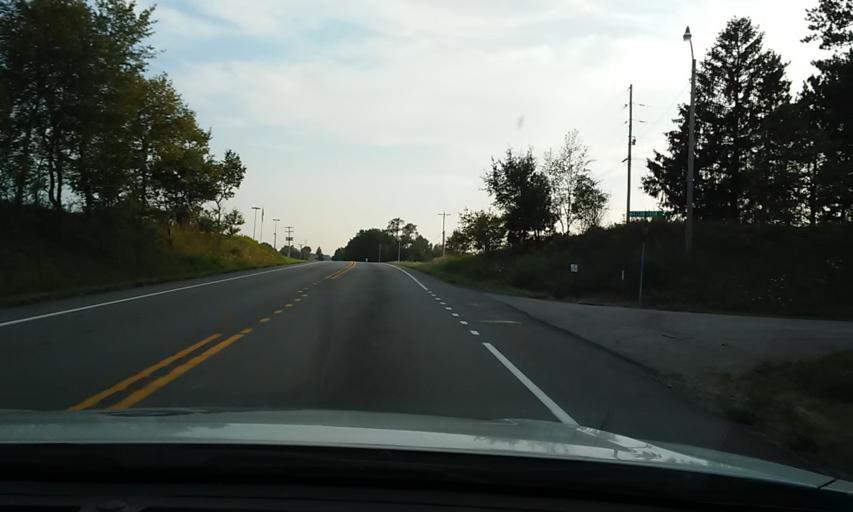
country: US
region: Pennsylvania
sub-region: Forest County
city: Marienville
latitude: 41.5420
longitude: -79.0378
